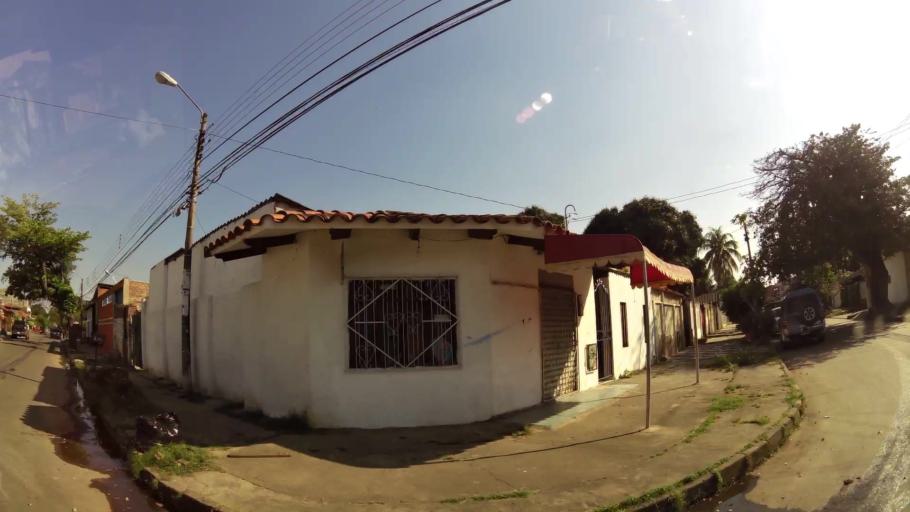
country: BO
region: Santa Cruz
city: Santa Cruz de la Sierra
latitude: -17.7831
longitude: -63.1616
